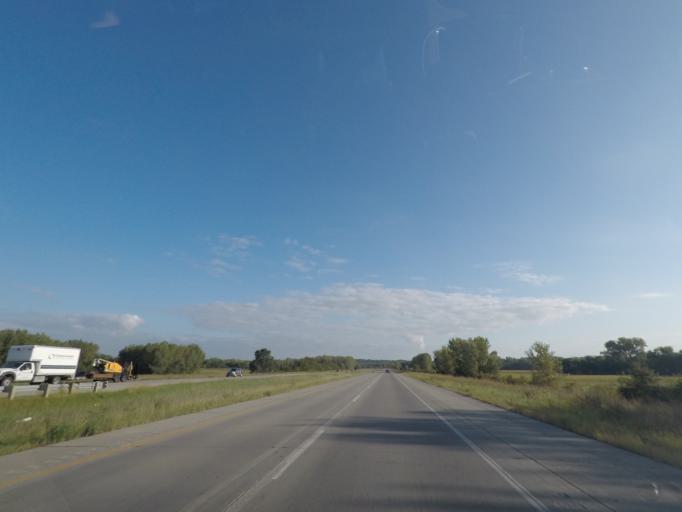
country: US
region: Iowa
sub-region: Polk County
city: Pleasant Hill
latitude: 41.5472
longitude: -93.5135
